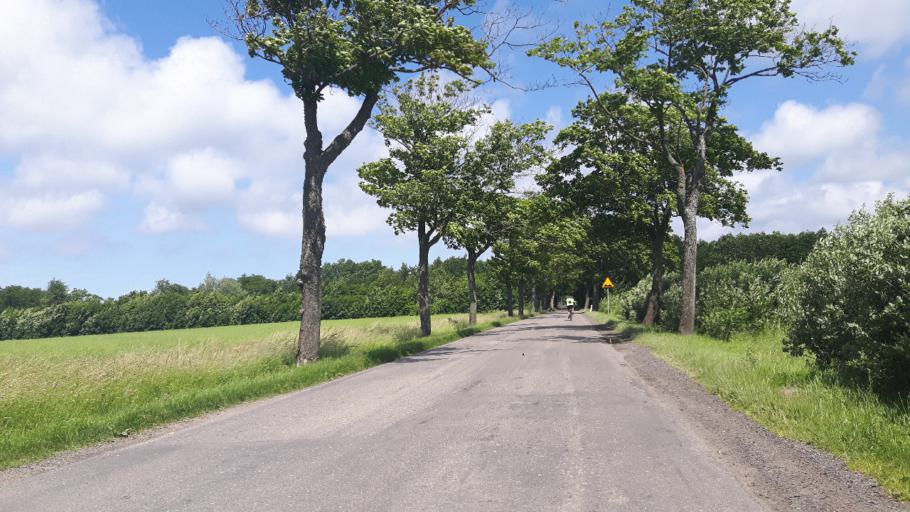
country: PL
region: Pomeranian Voivodeship
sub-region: Powiat slupski
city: Ustka
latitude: 54.5309
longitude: 16.8160
